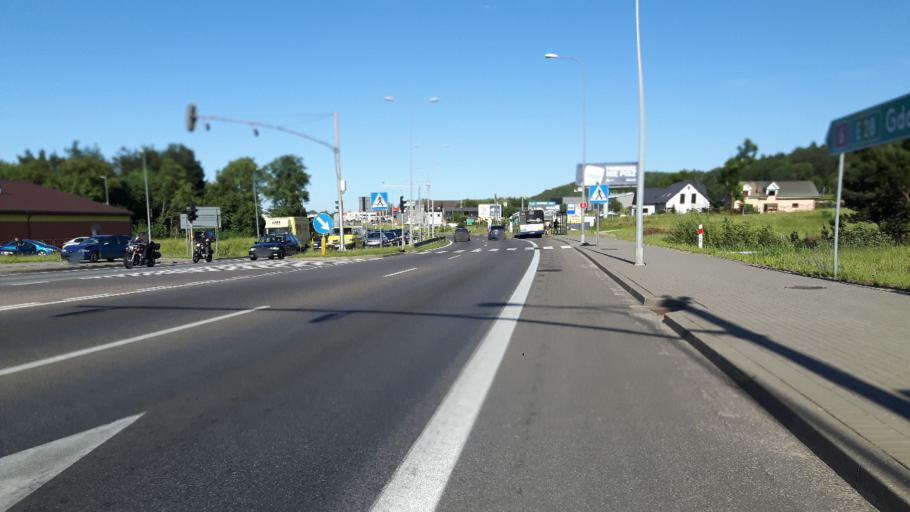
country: PL
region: Pomeranian Voivodeship
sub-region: Powiat wejherowski
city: Reda
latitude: 54.6028
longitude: 18.2995
